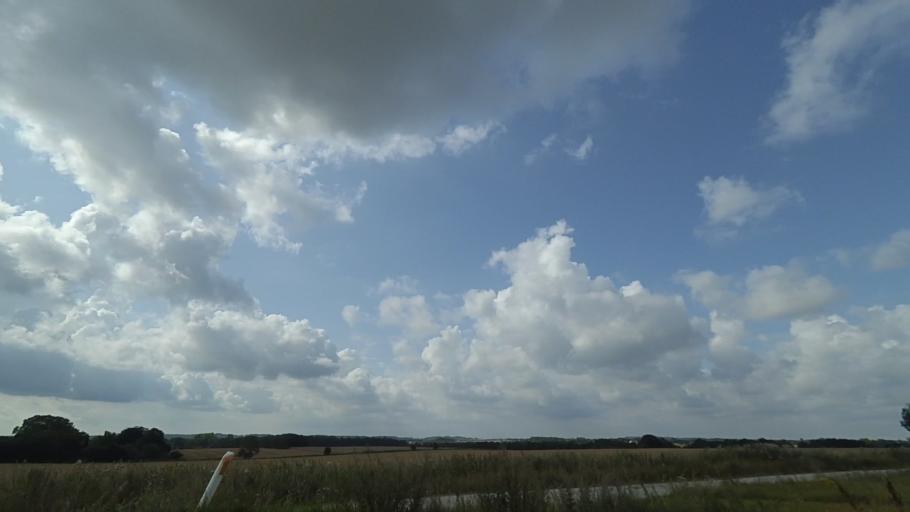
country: DK
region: Central Jutland
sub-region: Norddjurs Kommune
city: Auning
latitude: 56.4831
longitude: 10.4323
